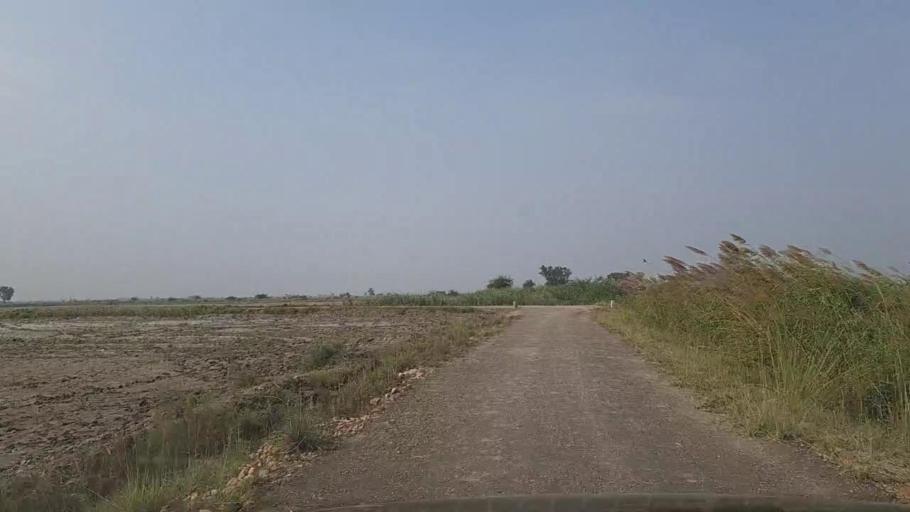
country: PK
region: Sindh
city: Thatta
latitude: 24.7638
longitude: 67.8501
